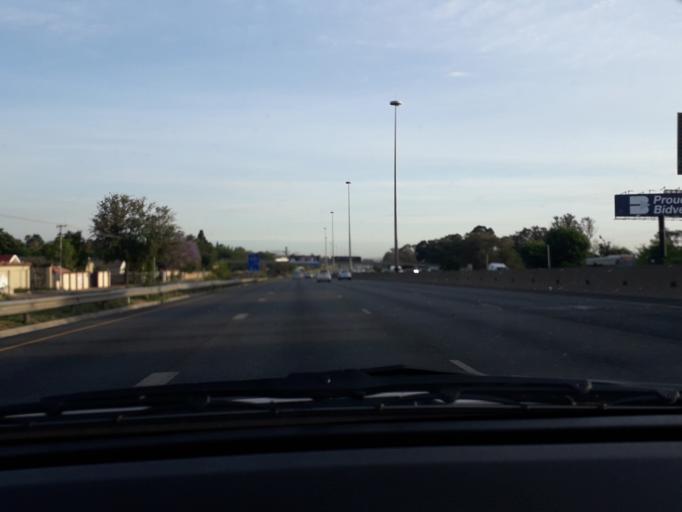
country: ZA
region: Gauteng
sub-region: City of Johannesburg Metropolitan Municipality
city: Modderfontein
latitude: -26.0794
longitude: 28.0872
